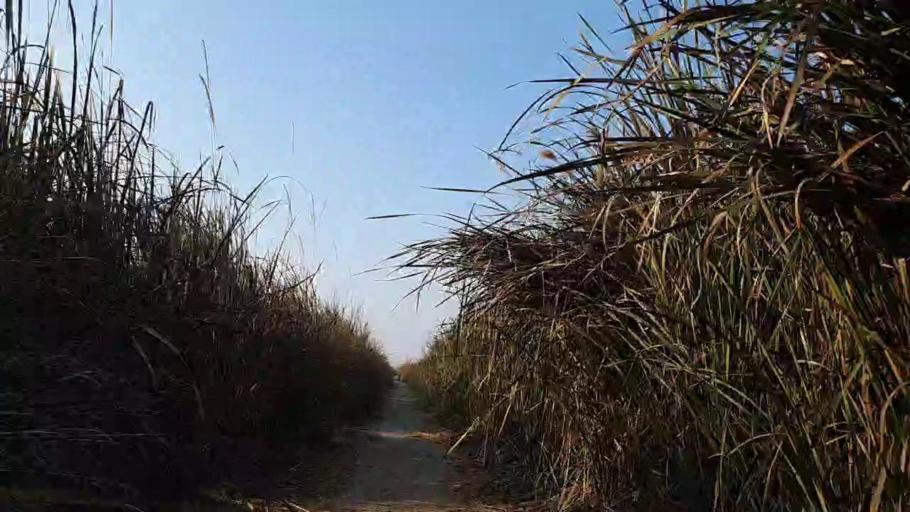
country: PK
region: Sindh
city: Sakrand
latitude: 26.0919
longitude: 68.3805
